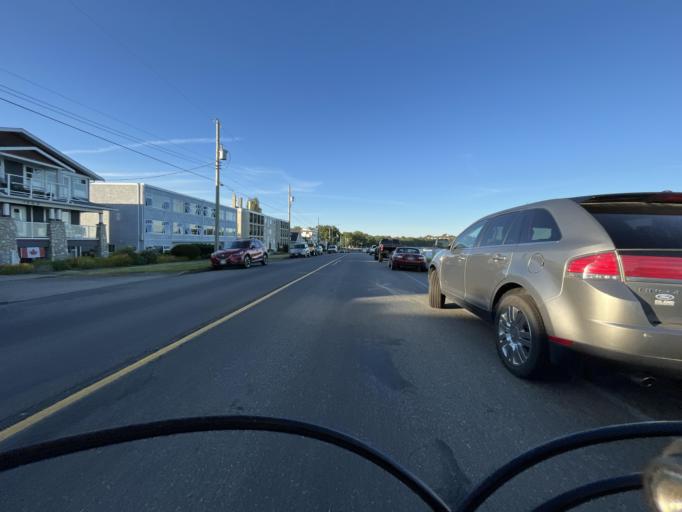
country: CA
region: British Columbia
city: Victoria
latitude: 48.4072
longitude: -123.3478
